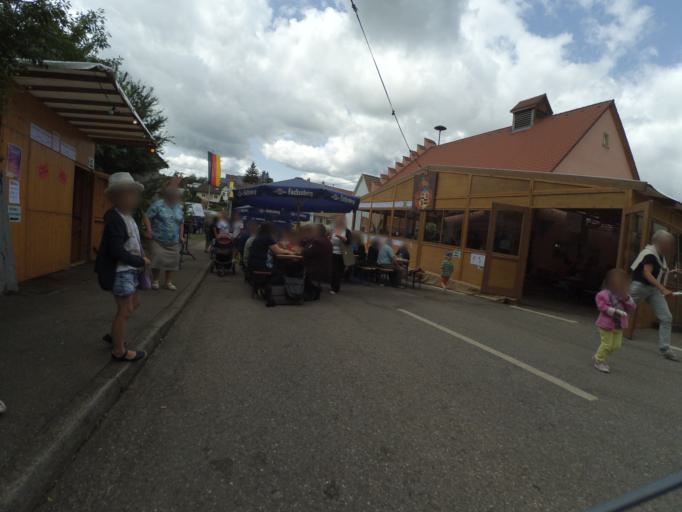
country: DE
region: Baden-Wuerttemberg
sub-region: Freiburg Region
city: Hufingen
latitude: 47.8916
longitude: 8.4901
